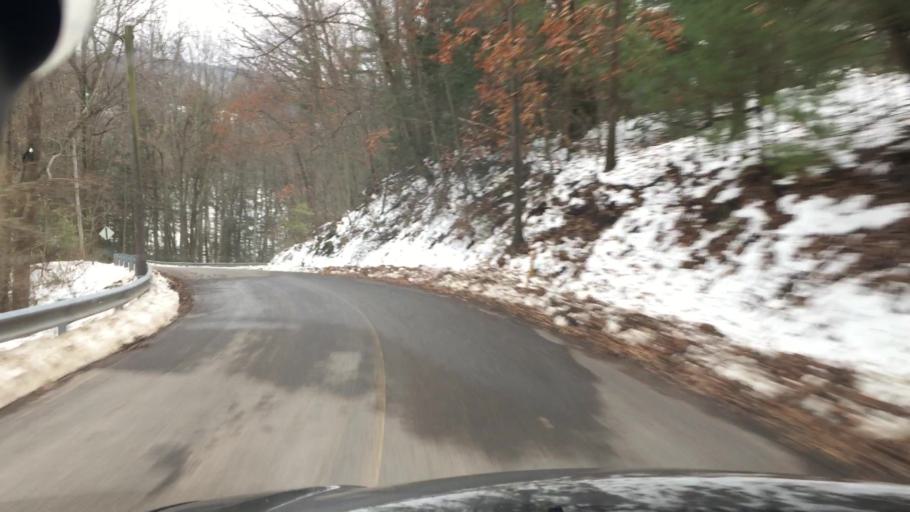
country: US
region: Pennsylvania
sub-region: Luzerne County
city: Conyngham
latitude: 41.0088
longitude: -76.1293
